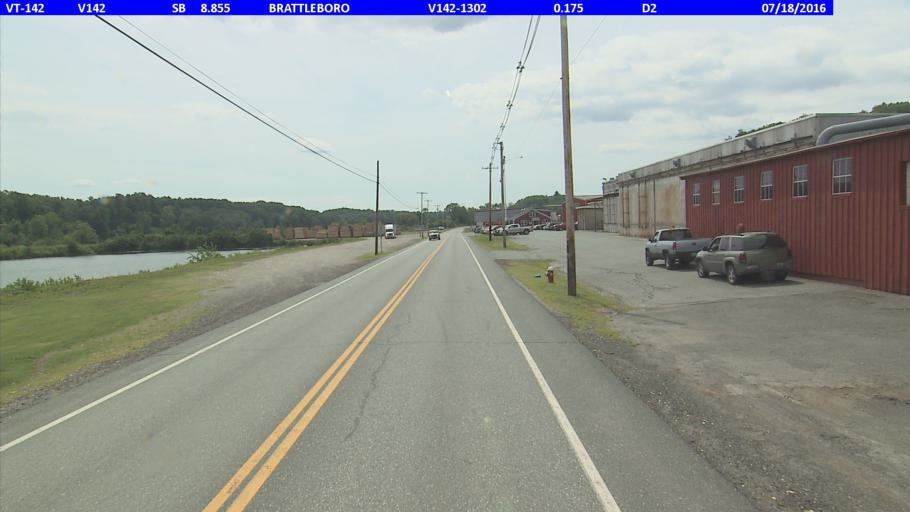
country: US
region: Vermont
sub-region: Windham County
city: Brattleboro
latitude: 42.8263
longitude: -72.5493
